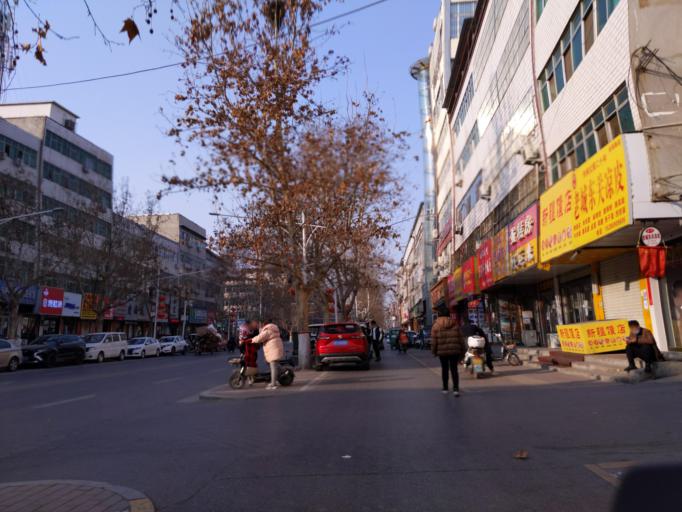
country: CN
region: Henan Sheng
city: Puyang
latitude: 35.7678
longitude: 115.0325
